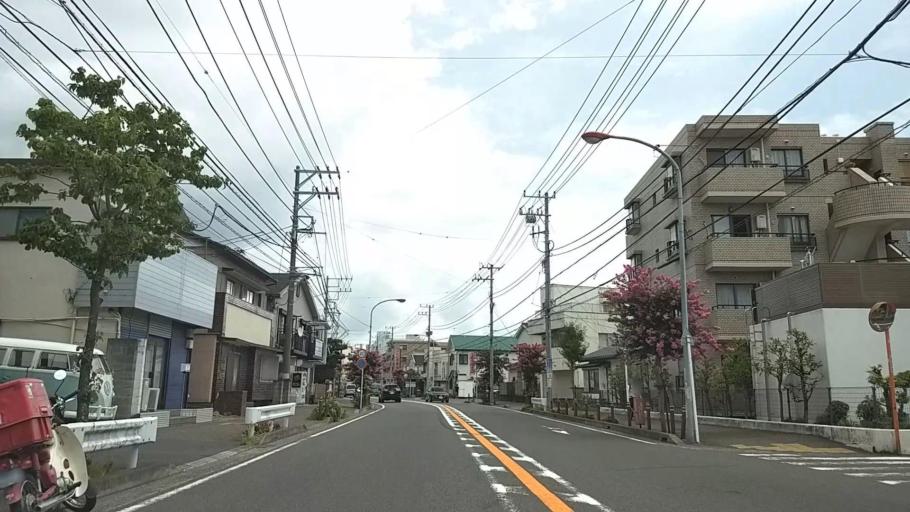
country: JP
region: Kanagawa
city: Fujisawa
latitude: 35.3470
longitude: 139.4703
